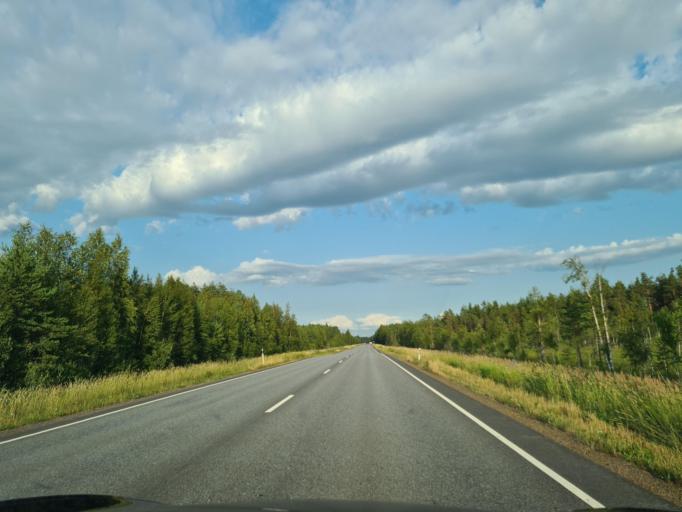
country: FI
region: Southern Ostrobothnia
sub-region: Seinaejoki
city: Lapua
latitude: 62.9912
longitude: 22.9067
